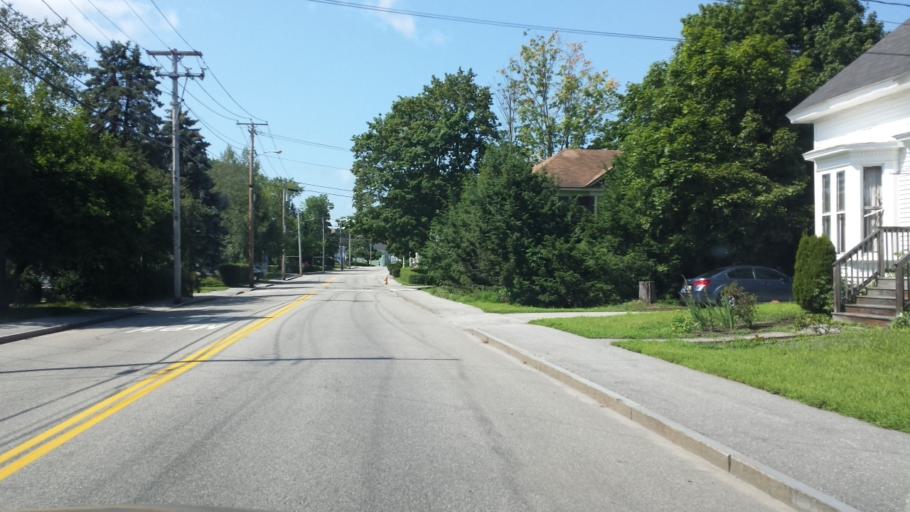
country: US
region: Maine
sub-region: York County
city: Biddeford
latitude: 43.4879
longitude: -70.4604
